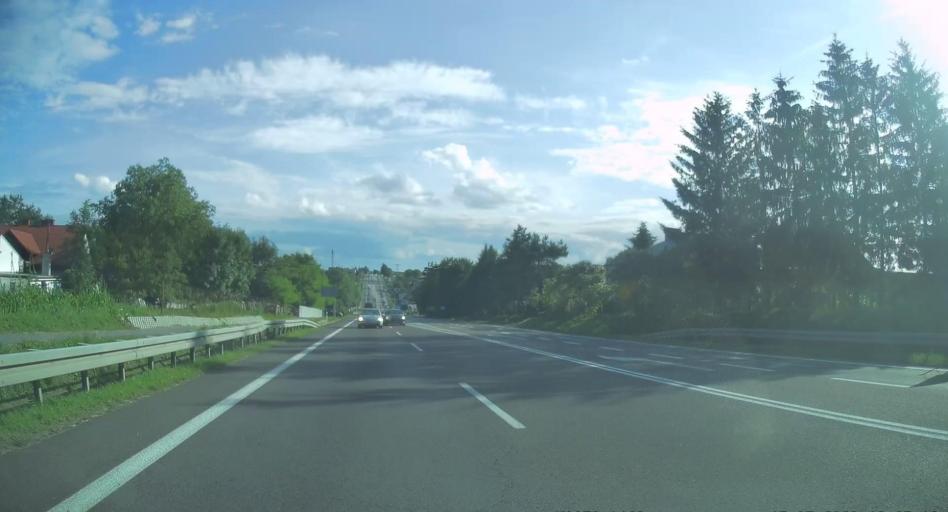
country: PL
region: Subcarpathian Voivodeship
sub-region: Powiat przemyski
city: Zurawica
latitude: 49.8259
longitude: 22.7906
